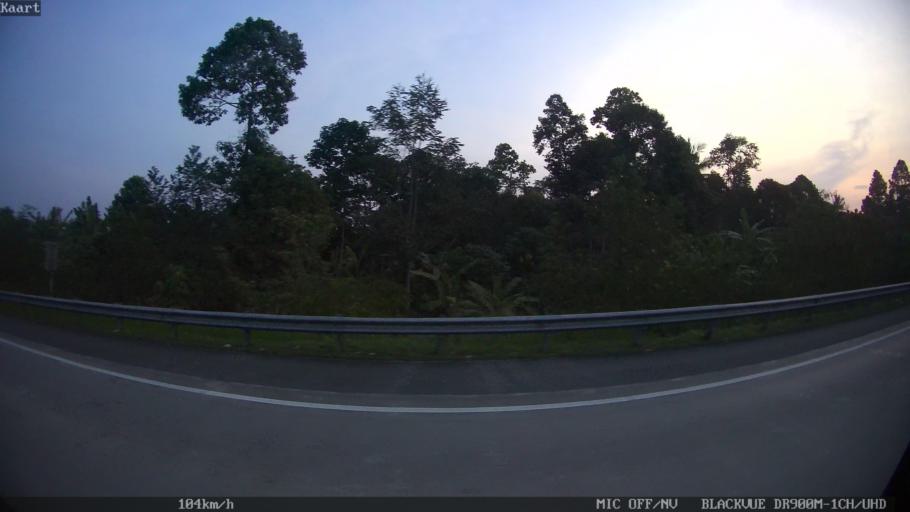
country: ID
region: Lampung
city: Pasuruan
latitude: -5.7110
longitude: 105.6478
